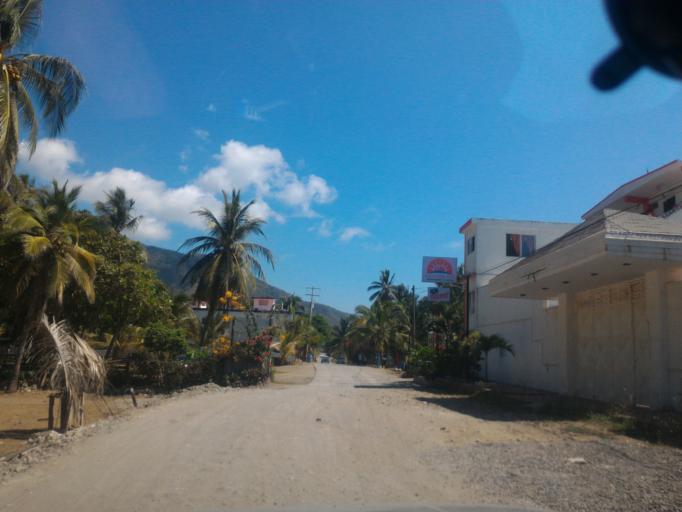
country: MX
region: Michoacan
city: Coahuayana Viejo
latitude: 18.5841
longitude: -103.6755
